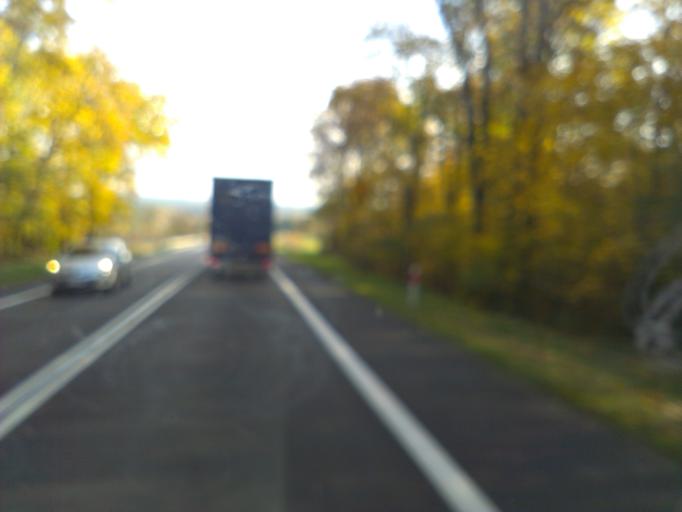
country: PL
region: Lubusz
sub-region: Powiat nowosolski
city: Bytom Odrzanski
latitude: 51.6625
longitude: 15.8194
